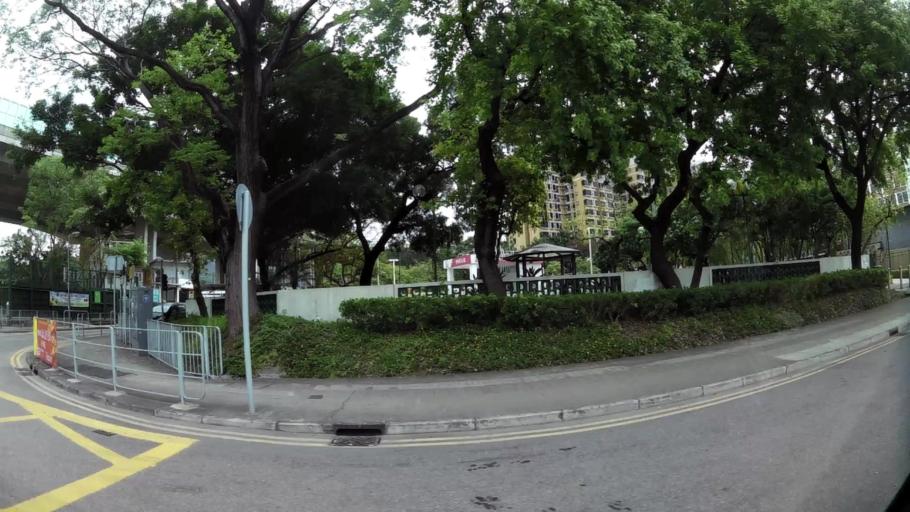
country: HK
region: Tuen Mun
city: Tuen Mun
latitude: 22.4214
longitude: 113.9846
